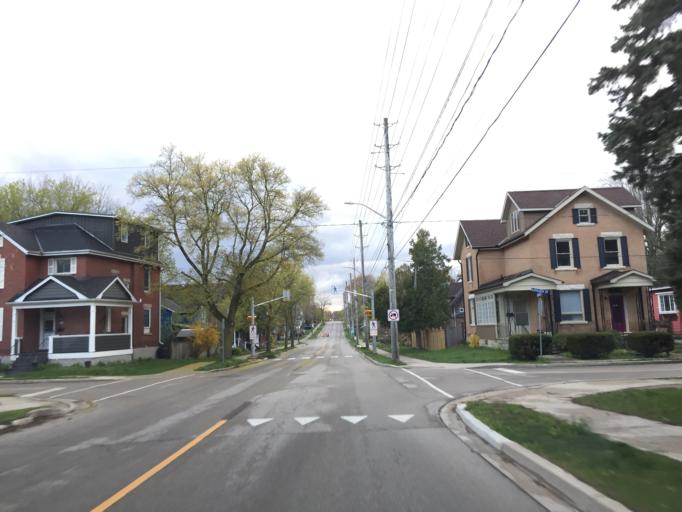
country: CA
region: Ontario
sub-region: Wellington County
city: Guelph
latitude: 43.5474
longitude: -80.2607
